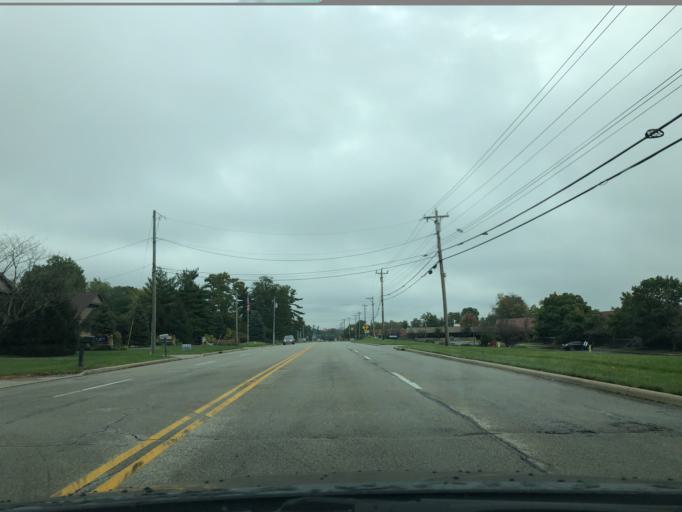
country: US
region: Ohio
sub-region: Hamilton County
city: Highpoint
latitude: 39.2803
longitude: -84.3532
